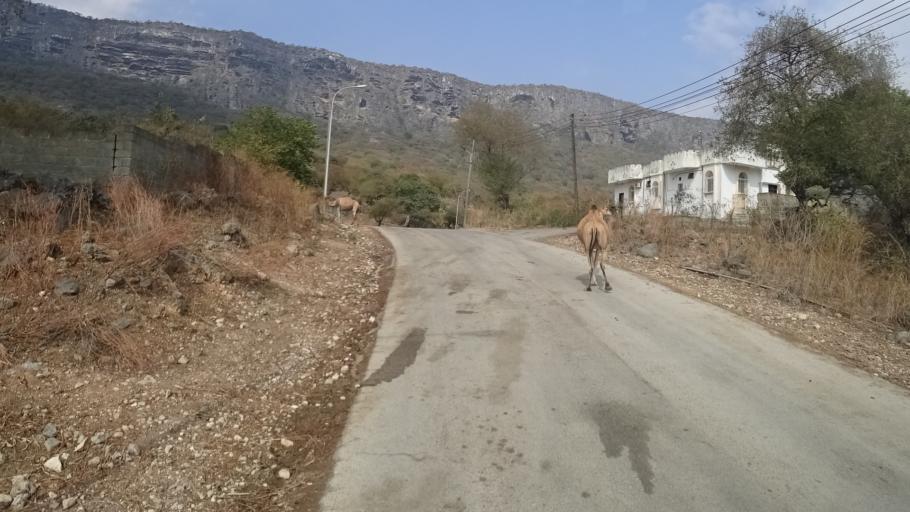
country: YE
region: Al Mahrah
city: Hawf
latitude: 16.7152
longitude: 53.2526
